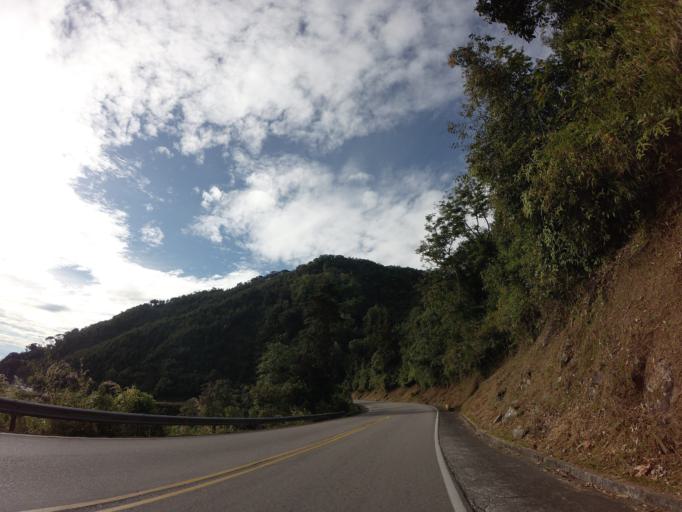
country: CO
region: Tolima
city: Herveo
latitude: 5.1441
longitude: -75.1525
